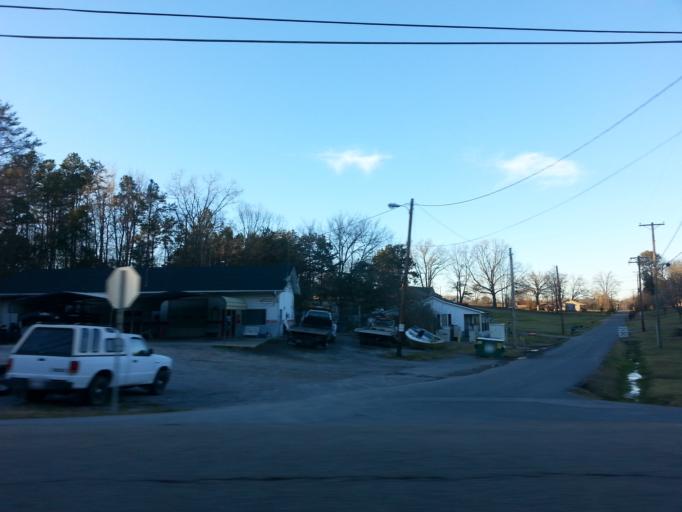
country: US
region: Tennessee
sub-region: Knox County
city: Mascot
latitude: 35.9866
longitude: -83.7988
